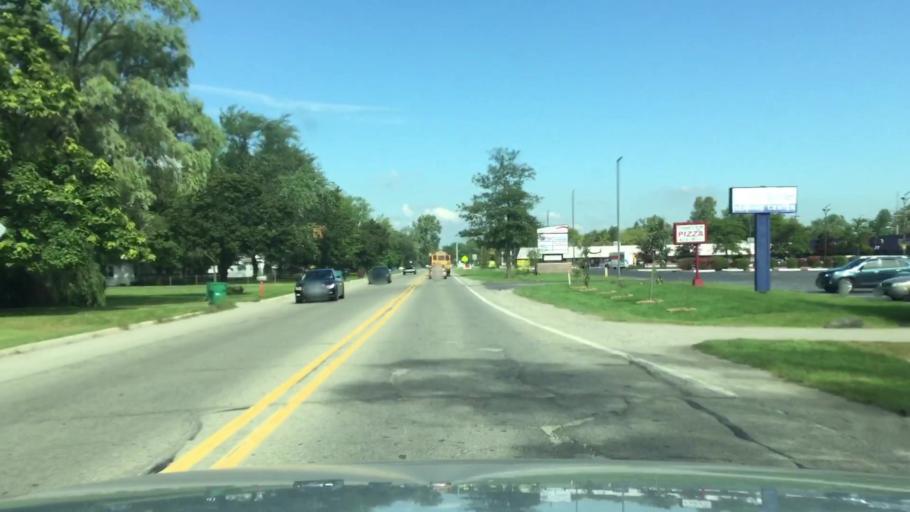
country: US
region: Michigan
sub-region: Wayne County
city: Belleville
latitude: 42.1941
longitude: -83.4842
